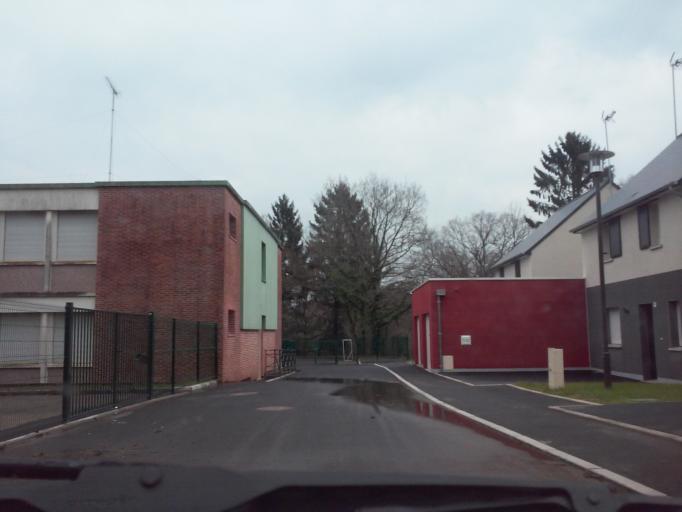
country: FR
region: Brittany
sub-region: Departement d'Ille-et-Vilaine
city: Fougeres
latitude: 48.3663
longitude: -1.1786
